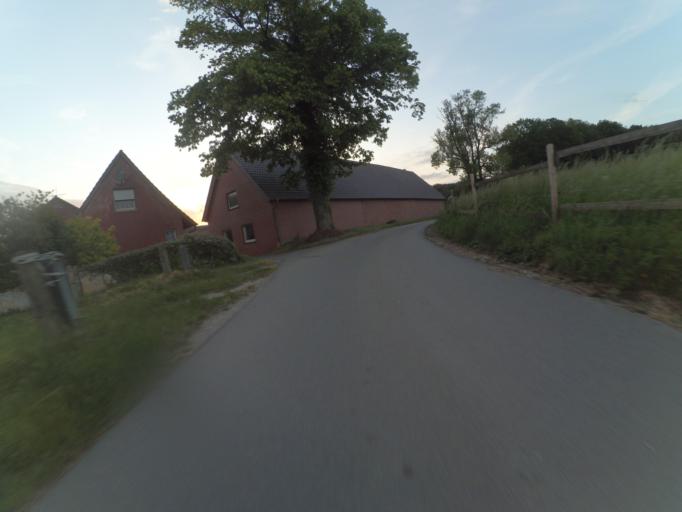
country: DE
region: North Rhine-Westphalia
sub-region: Regierungsbezirk Munster
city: Tecklenburg
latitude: 52.2495
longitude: 7.8028
